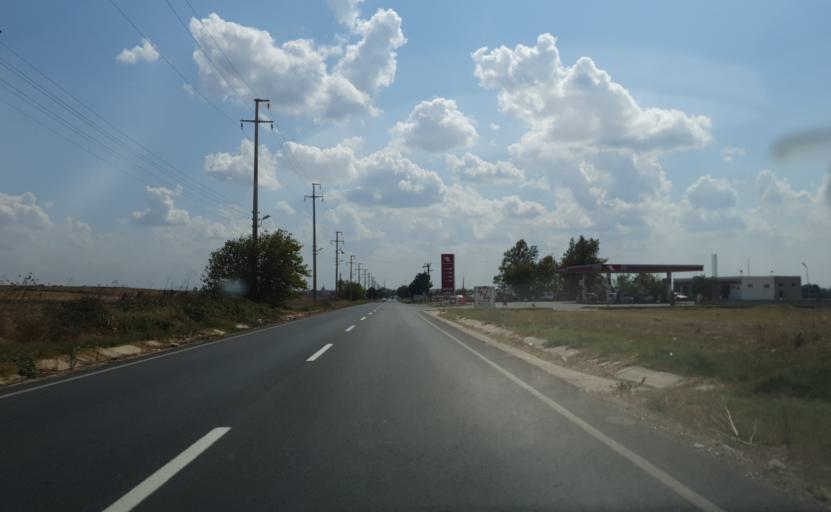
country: TR
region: Kirklareli
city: Luleburgaz
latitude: 41.3733
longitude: 27.3411
